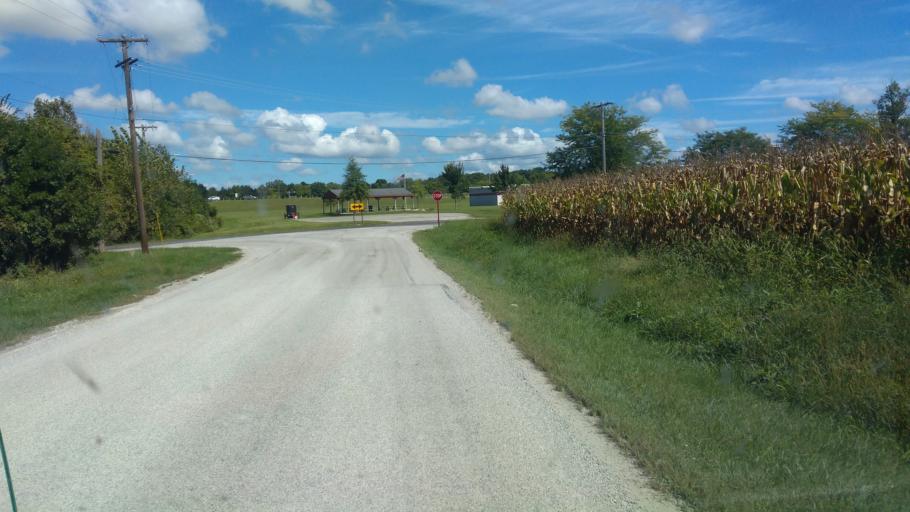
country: US
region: Ohio
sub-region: Richland County
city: Shelby
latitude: 40.9079
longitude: -82.6544
